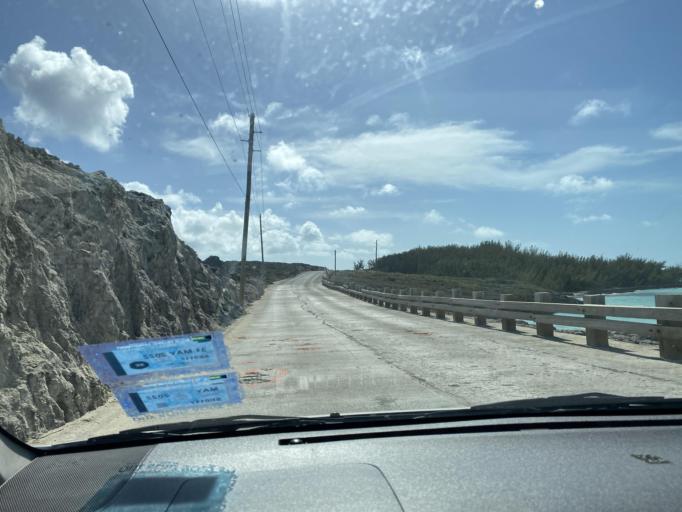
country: BS
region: Harbour Island
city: Dunmore Town
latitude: 25.4371
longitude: -76.6035
